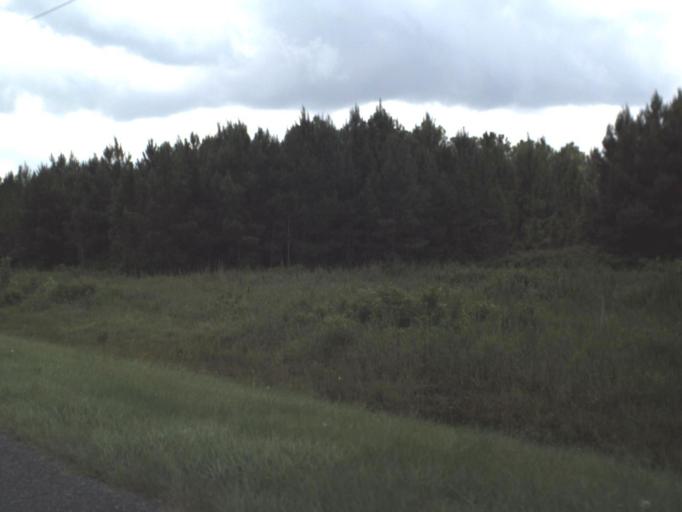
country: US
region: Florida
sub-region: Levy County
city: Bronson
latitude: 29.4714
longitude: -82.6760
